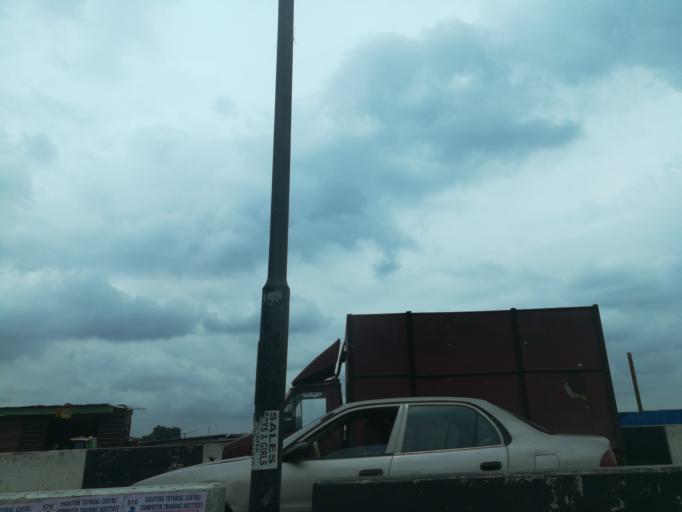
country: NG
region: Lagos
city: Ojota
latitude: 6.6131
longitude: 3.3968
